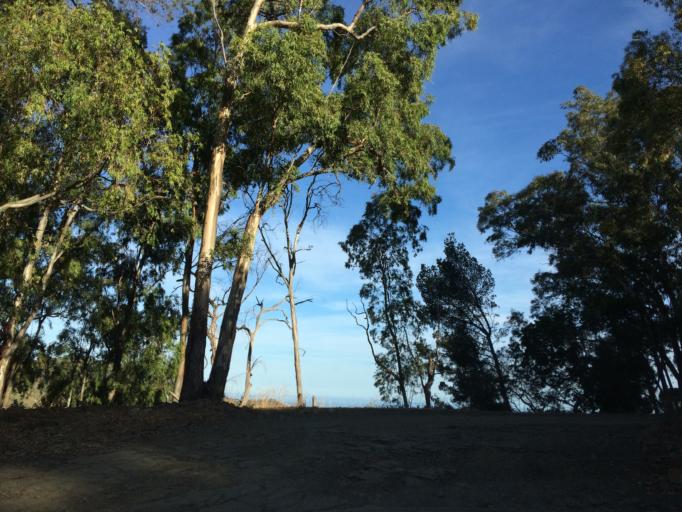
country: ES
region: Andalusia
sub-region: Provincia de Malaga
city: Totalan
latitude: 36.7869
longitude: -4.3204
